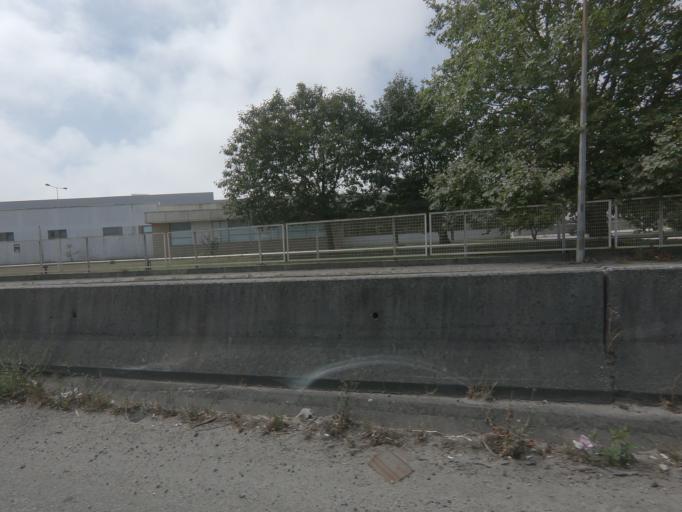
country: PT
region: Porto
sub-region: Matosinhos
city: Santa Cruz do Bispo
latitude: 41.2169
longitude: -8.6873
